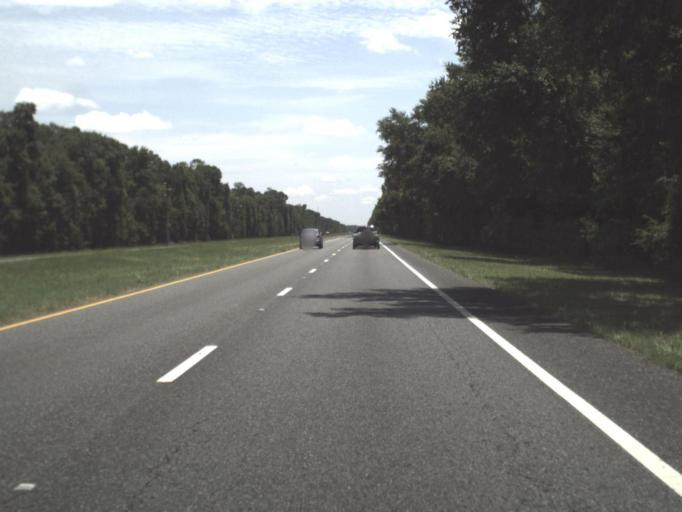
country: US
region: Florida
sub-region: Dixie County
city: Cross City
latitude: 29.6601
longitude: -83.1959
